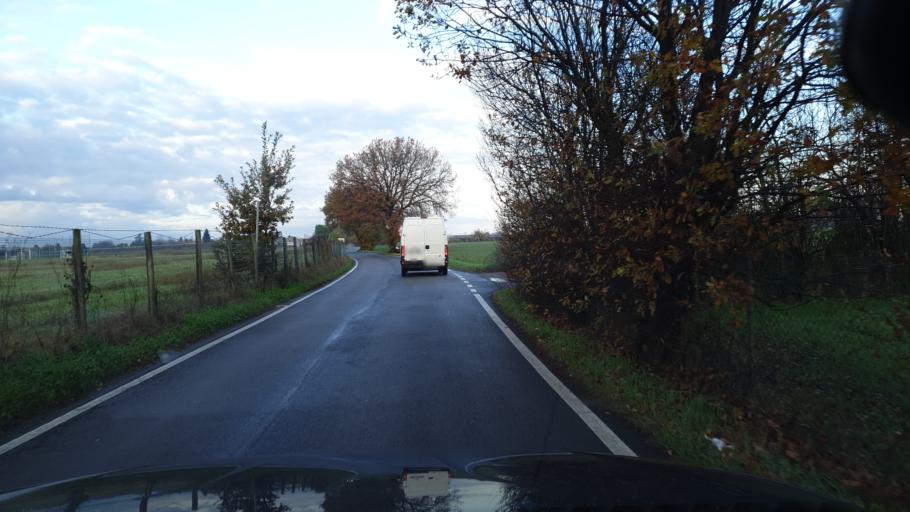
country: IT
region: Emilia-Romagna
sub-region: Provincia di Bologna
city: Crespellano
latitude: 44.5195
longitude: 11.1296
